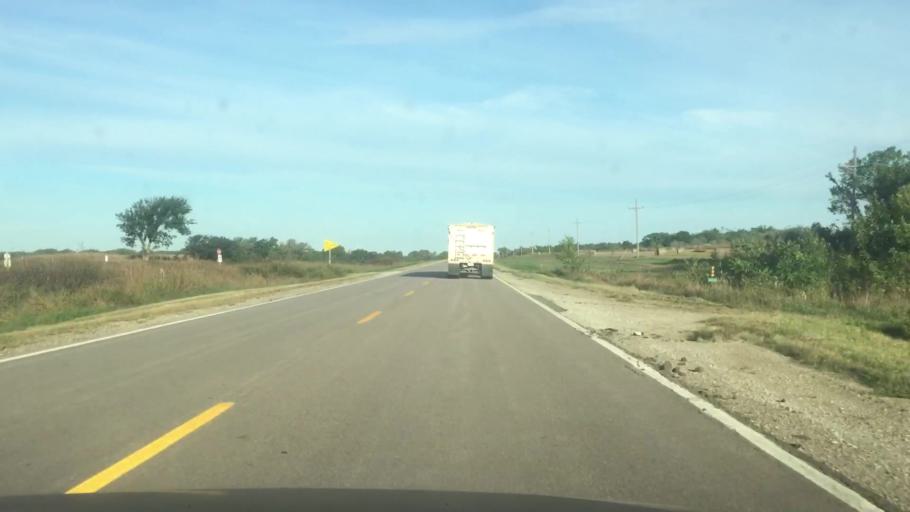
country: US
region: Nebraska
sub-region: Jefferson County
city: Fairbury
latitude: 40.0555
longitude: -97.0388
